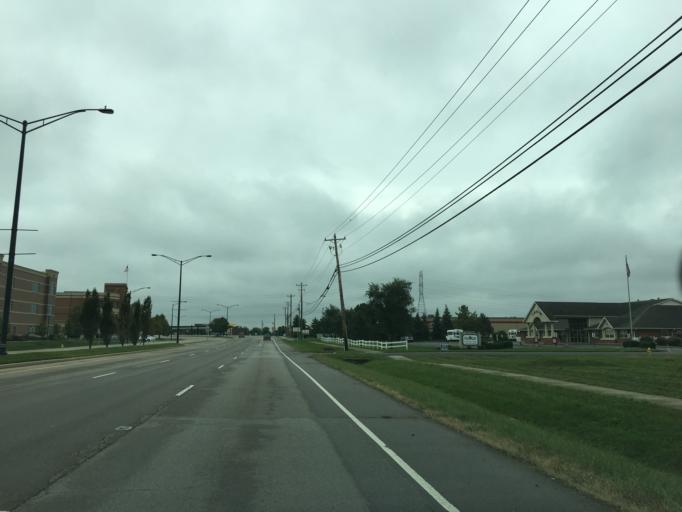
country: US
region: Ohio
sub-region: Butler County
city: Beckett Ridge
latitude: 39.3289
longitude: -84.4353
